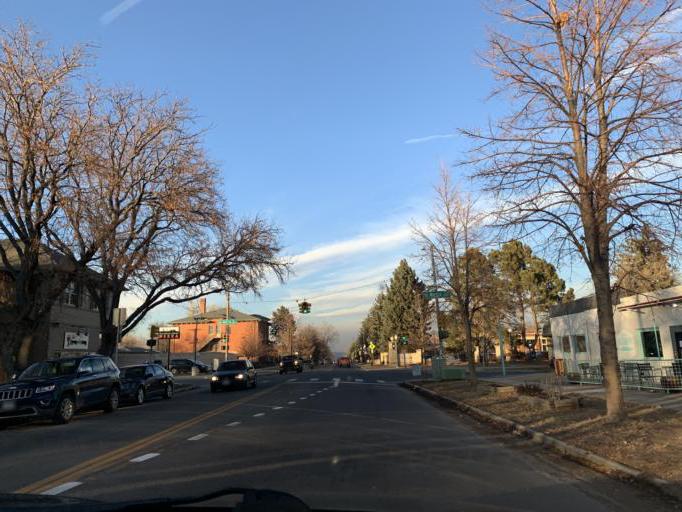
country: US
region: Colorado
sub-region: Adams County
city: Berkley
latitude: 39.7870
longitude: -105.0346
